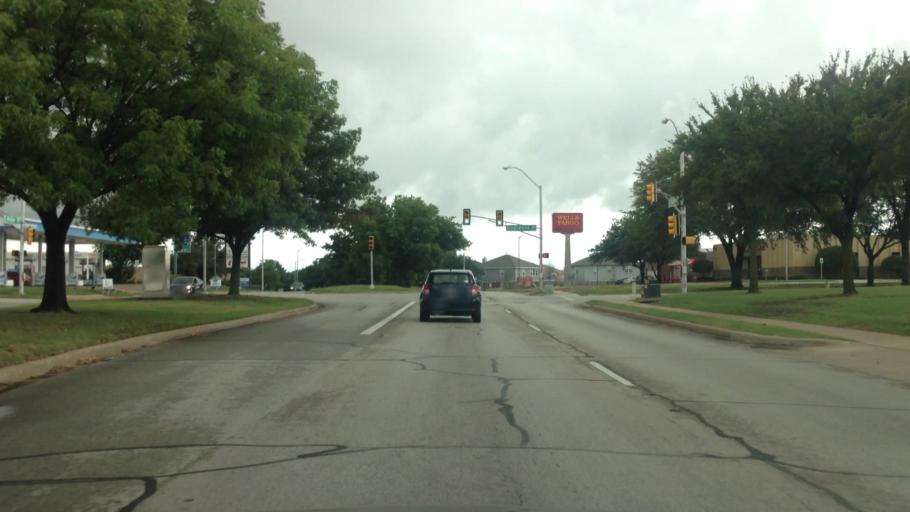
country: US
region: Texas
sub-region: Tarrant County
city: Edgecliff Village
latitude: 32.6414
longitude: -97.3960
